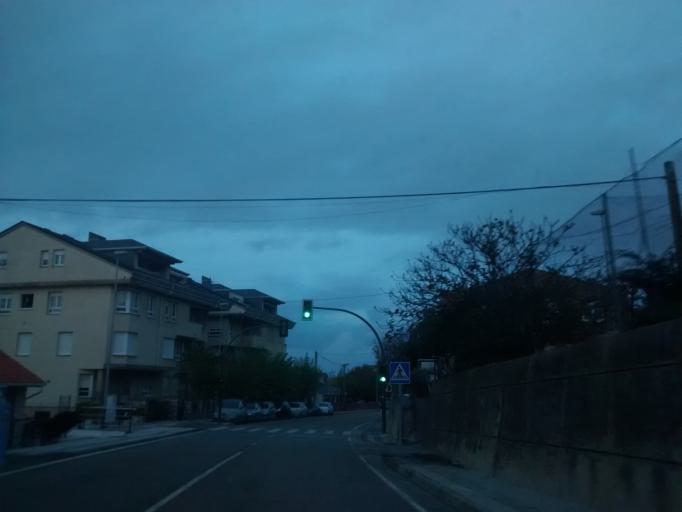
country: ES
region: Cantabria
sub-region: Provincia de Cantabria
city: Santa Cruz de Bezana
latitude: 43.4579
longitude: -3.9312
